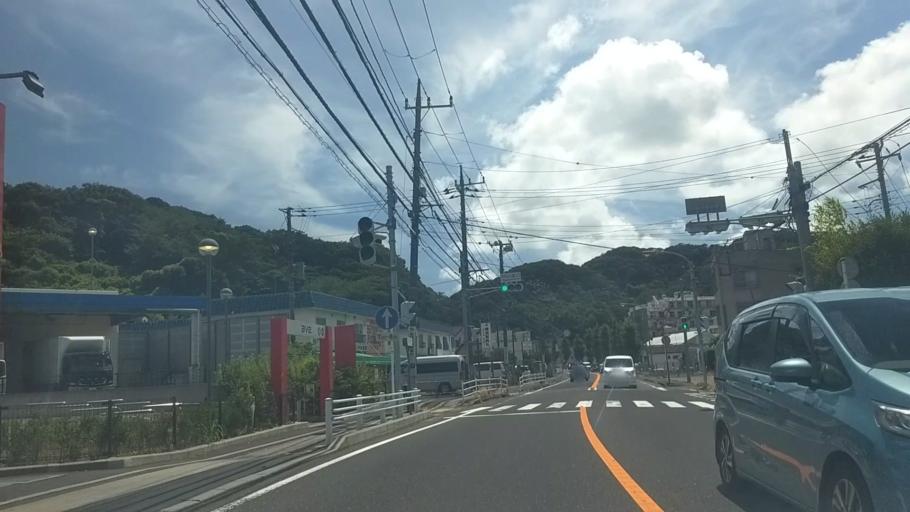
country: JP
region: Kanagawa
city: Yokosuka
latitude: 35.2519
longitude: 139.6658
